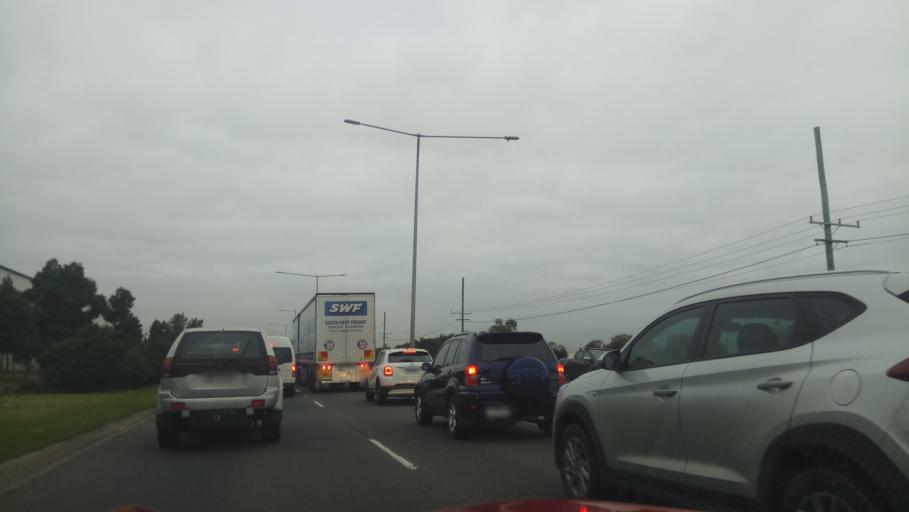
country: AU
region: Victoria
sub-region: Hobsons Bay
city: Altona North
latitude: -37.8441
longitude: 144.8249
